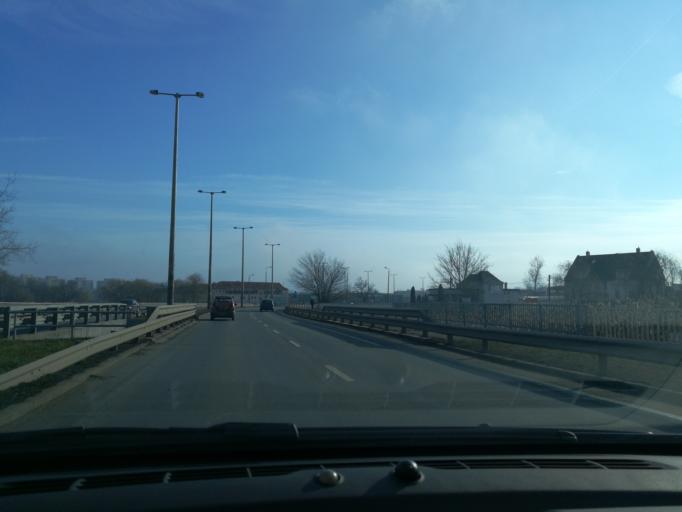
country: HU
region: Szabolcs-Szatmar-Bereg
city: Nyiregyhaza
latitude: 47.9611
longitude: 21.7274
